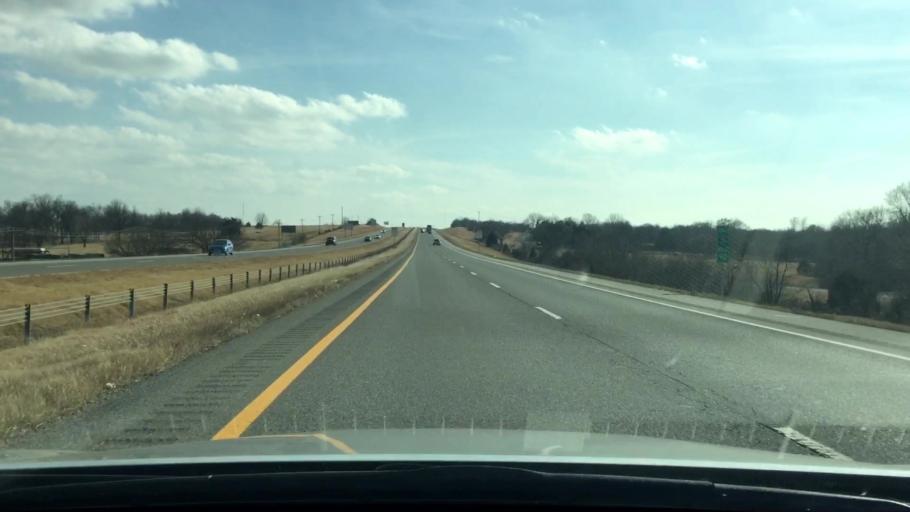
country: US
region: Oklahoma
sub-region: McClain County
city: Purcell
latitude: 34.9717
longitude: -97.3710
